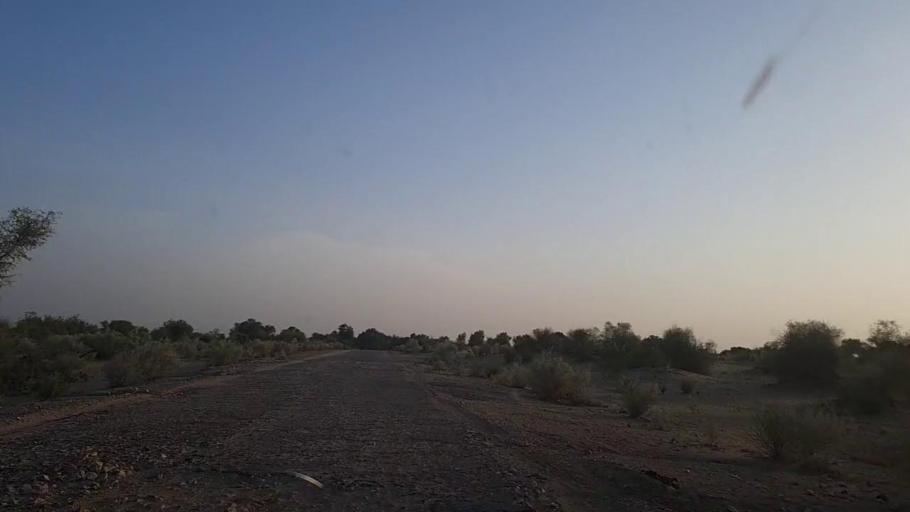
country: PK
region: Sindh
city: Khanpur
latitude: 27.6147
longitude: 69.4398
